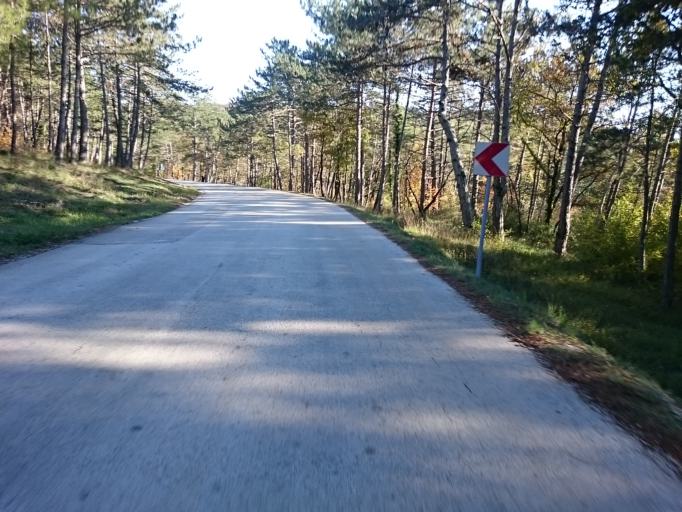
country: HR
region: Istarska
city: Buje
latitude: 45.3919
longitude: 13.7166
